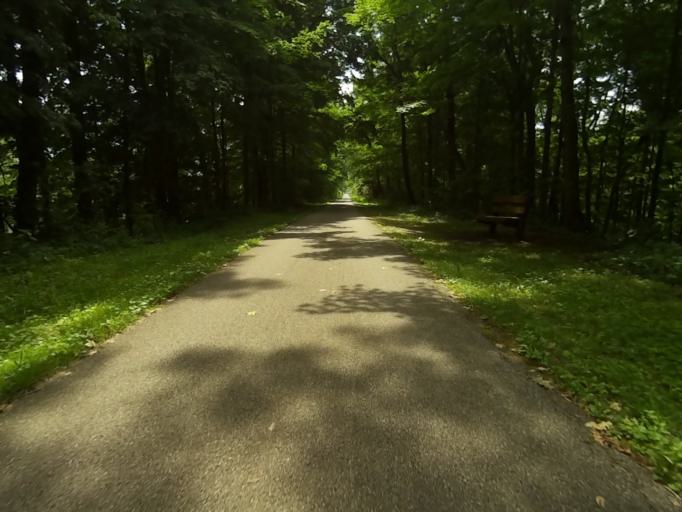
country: US
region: Ohio
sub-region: Summit County
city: Hudson
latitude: 41.2115
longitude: -81.4602
